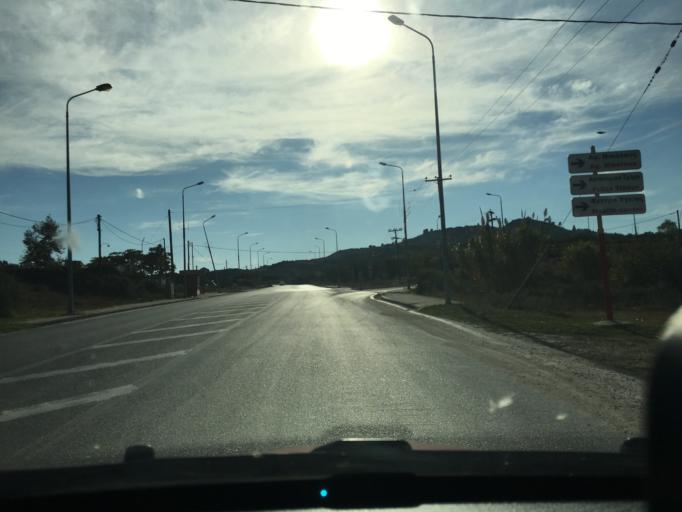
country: GR
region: Central Macedonia
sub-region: Nomos Chalkidikis
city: Agios Nikolaos
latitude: 40.2463
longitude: 23.7104
